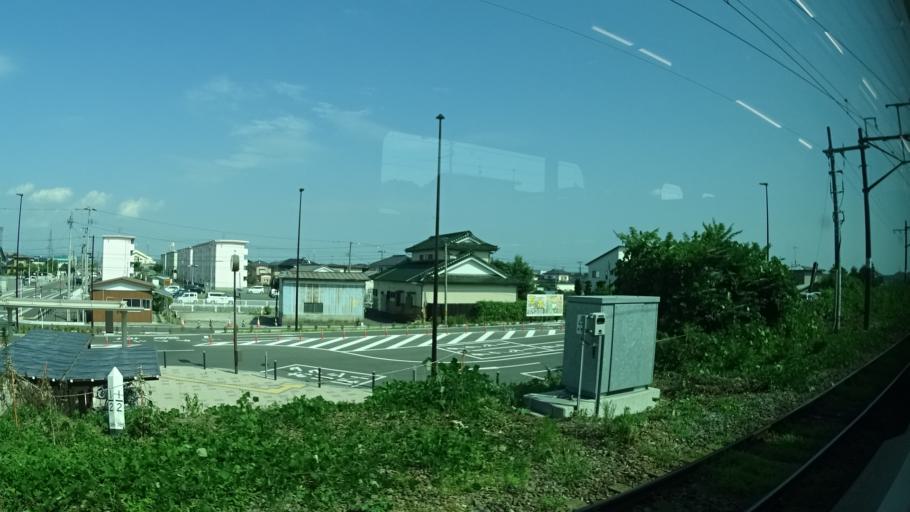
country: JP
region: Miyagi
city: Wakuya
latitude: 38.4744
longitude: 141.0981
